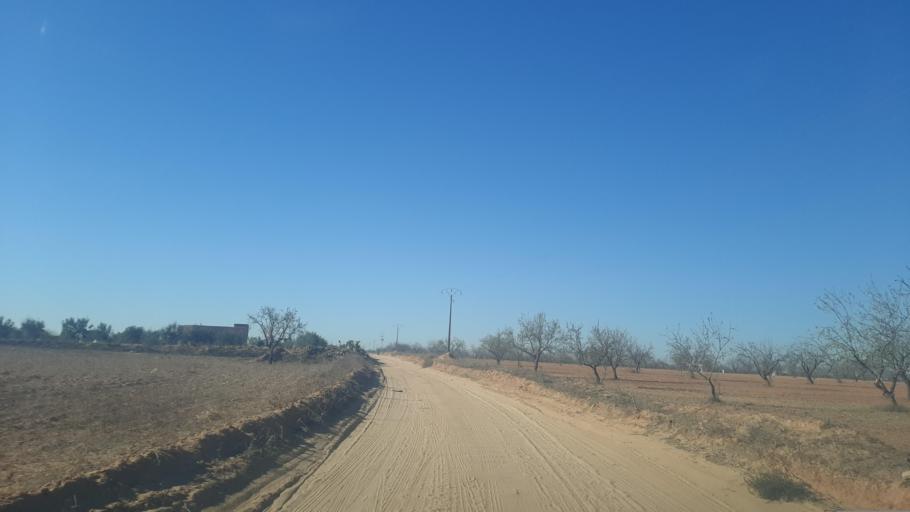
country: TN
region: Safaqis
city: Sfax
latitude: 34.8892
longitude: 10.5893
